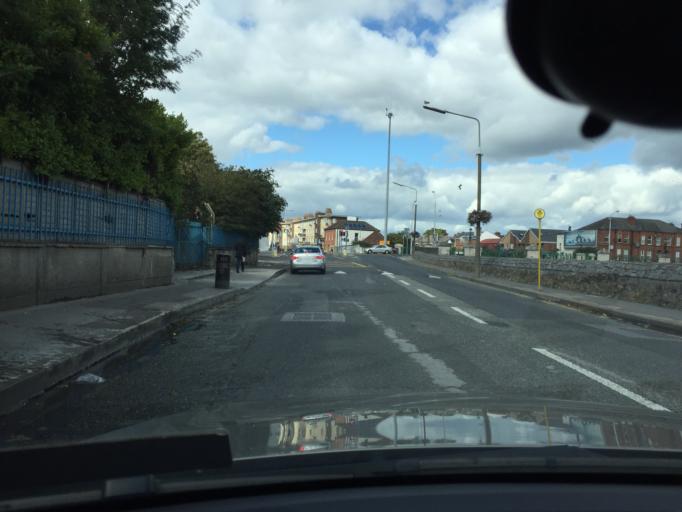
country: IE
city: Fairview
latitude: 53.3600
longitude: -6.2380
